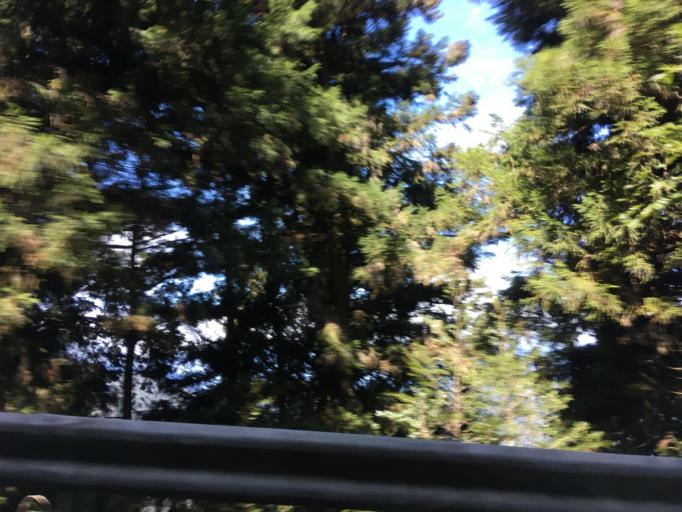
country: TW
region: Taiwan
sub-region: Yilan
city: Yilan
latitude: 24.5106
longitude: 121.5233
